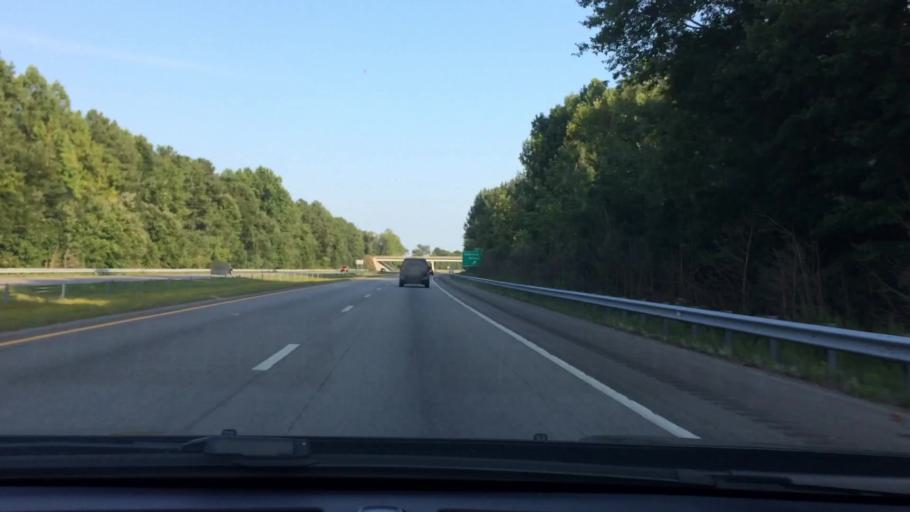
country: US
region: North Carolina
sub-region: Wilson County
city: Lucama
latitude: 35.6994
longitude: -77.9788
